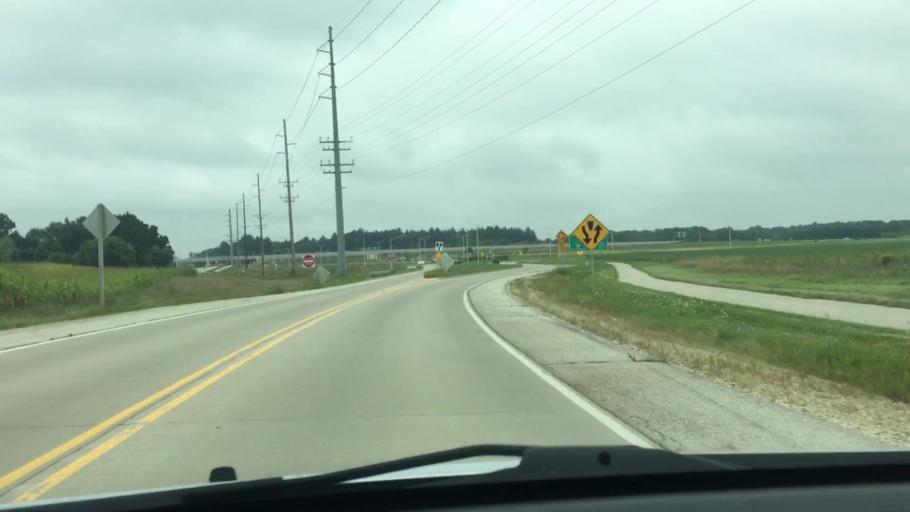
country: US
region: Wisconsin
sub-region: Waukesha County
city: Delafield
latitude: 43.0670
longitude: -88.4423
